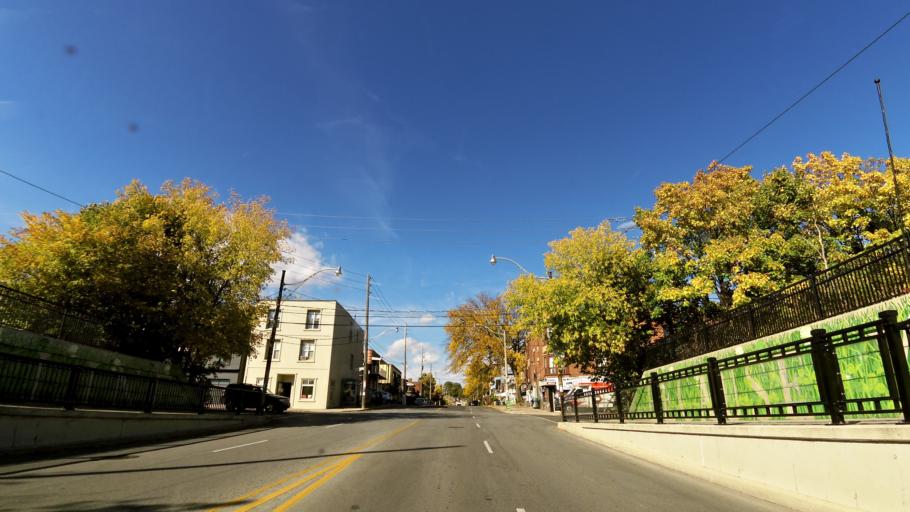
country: CA
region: Ontario
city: Toronto
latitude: 43.6704
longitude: -79.4330
